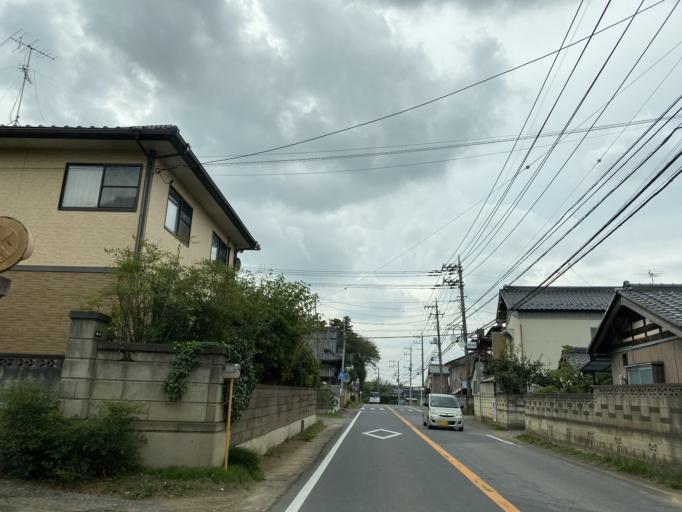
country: JP
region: Ibaraki
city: Mitsukaido
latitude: 35.9887
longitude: 140.0437
